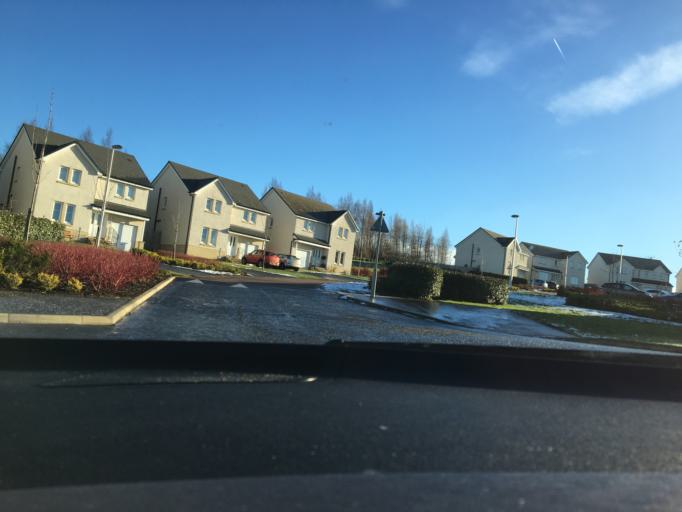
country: GB
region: Scotland
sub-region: Midlothian
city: Dalkeith
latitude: 55.8967
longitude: -3.0382
